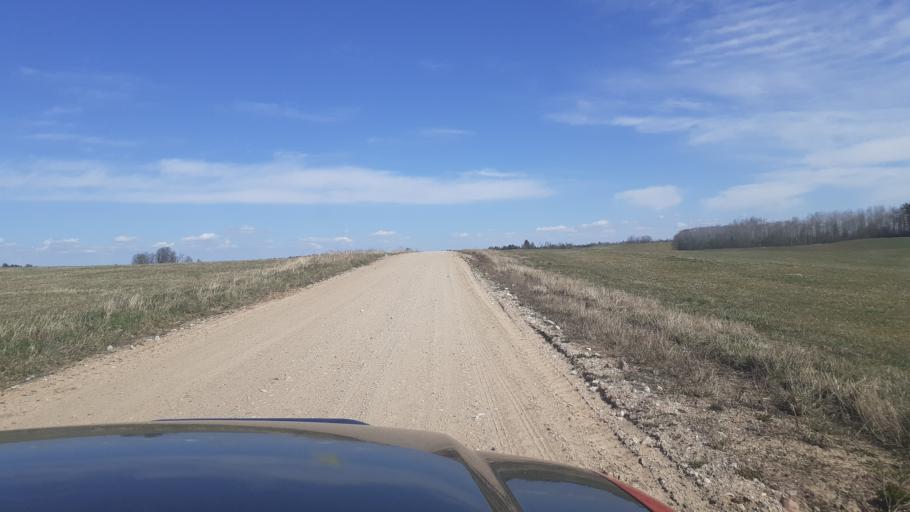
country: LV
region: Kuldigas Rajons
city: Kuldiga
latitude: 56.8491
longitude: 21.9908
